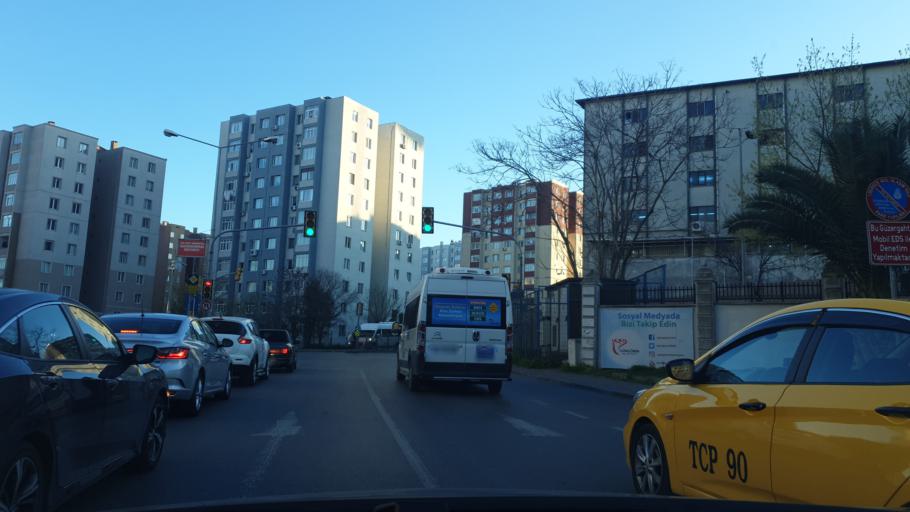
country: TR
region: Istanbul
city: merter keresteciler
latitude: 41.0091
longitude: 28.8751
